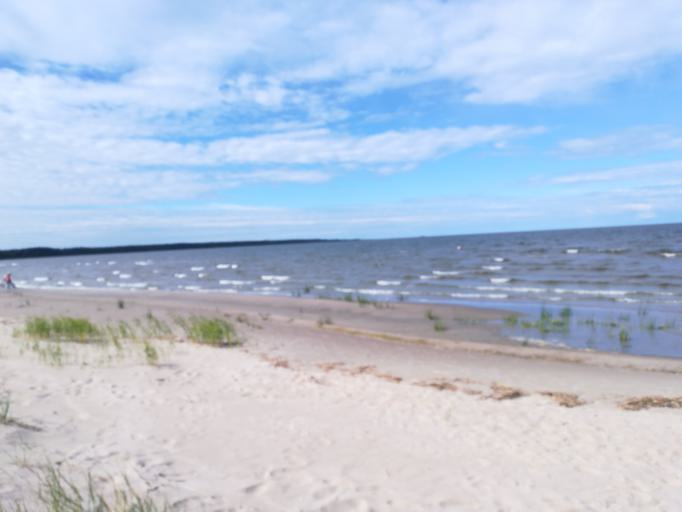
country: RU
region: Leningrad
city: Ust'-Luga
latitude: 59.6796
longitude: 28.2380
